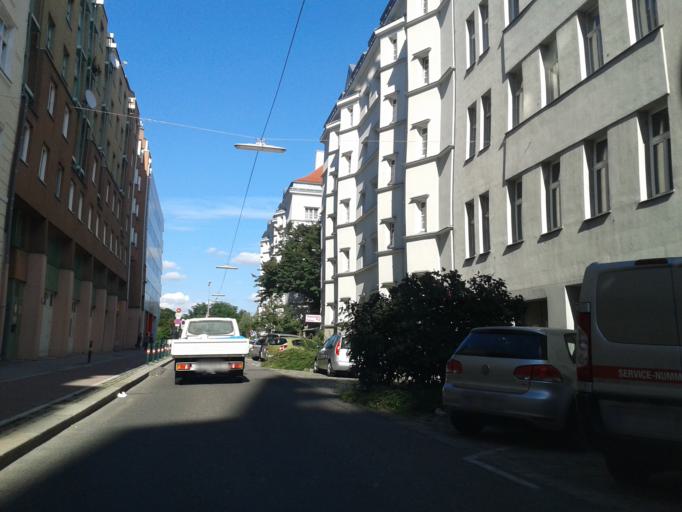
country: AT
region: Vienna
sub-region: Wien Stadt
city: Vienna
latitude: 48.1980
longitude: 16.4068
